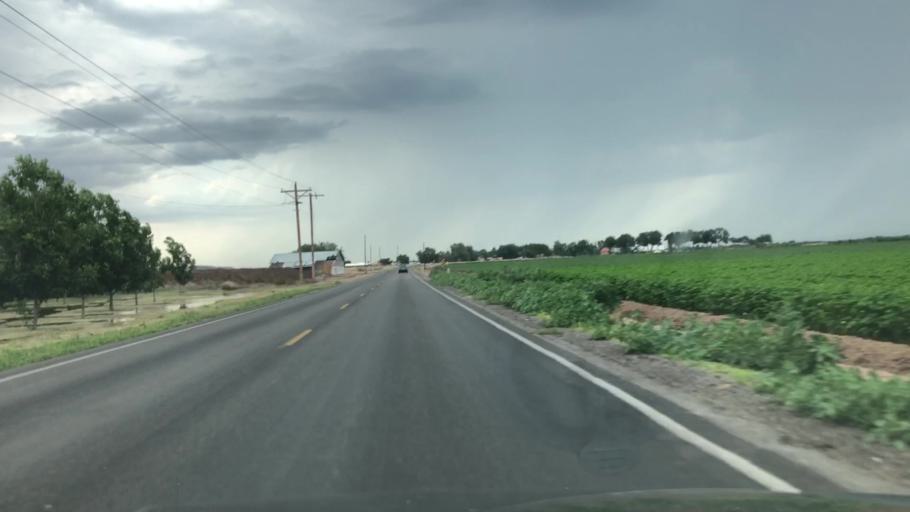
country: US
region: New Mexico
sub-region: Dona Ana County
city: Anthony
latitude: 32.0221
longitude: -106.6703
